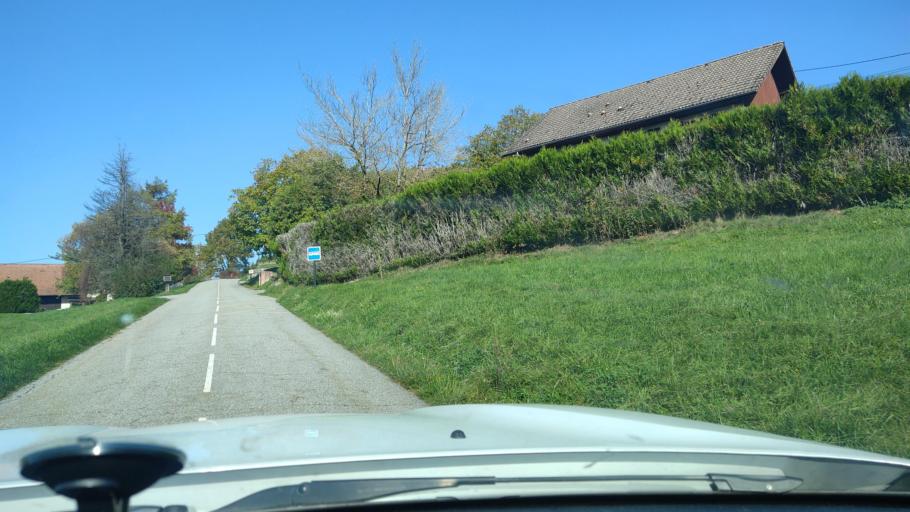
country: FR
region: Rhone-Alpes
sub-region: Departement de la Savoie
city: Les Echelles
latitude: 45.4616
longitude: 5.7611
